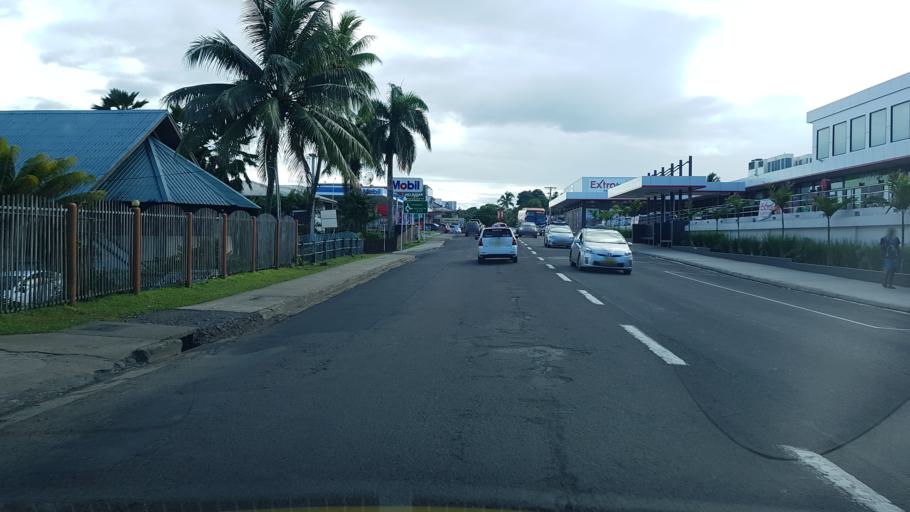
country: FJ
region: Central
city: Suva
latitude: -18.1450
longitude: 178.4346
